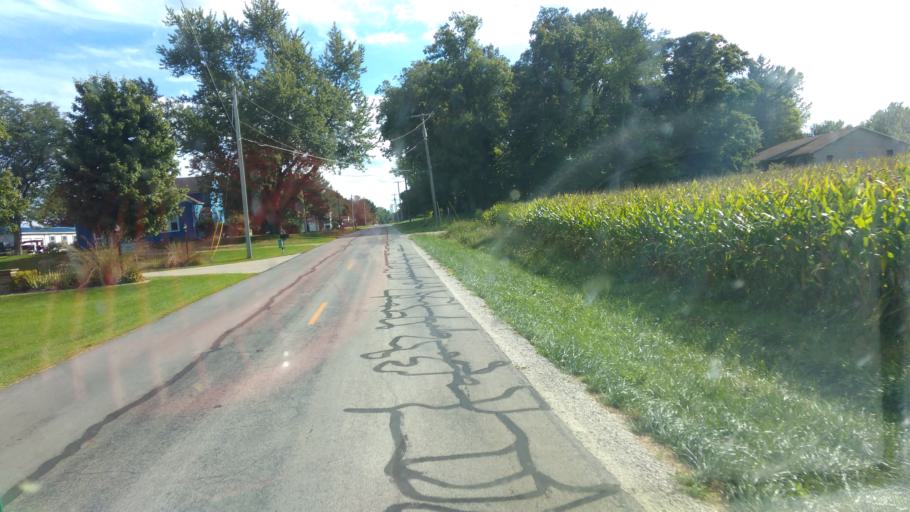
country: US
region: Ohio
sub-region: Sandusky County
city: Clyde
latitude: 41.2996
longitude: -83.0088
